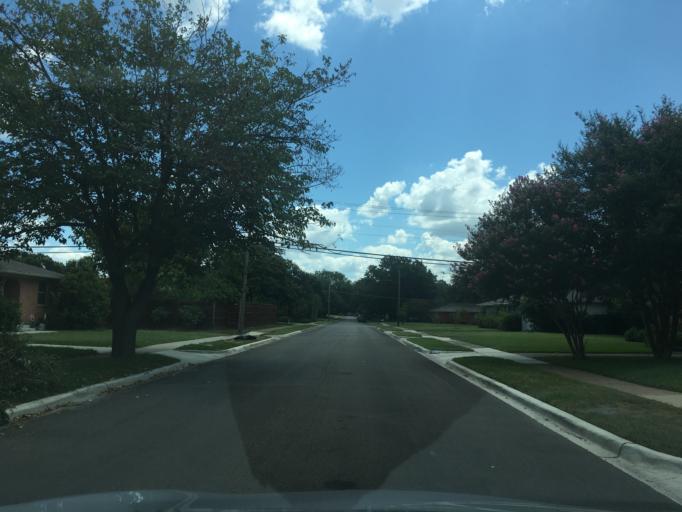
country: US
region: Texas
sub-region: Dallas County
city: Richardson
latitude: 32.8683
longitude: -96.7088
